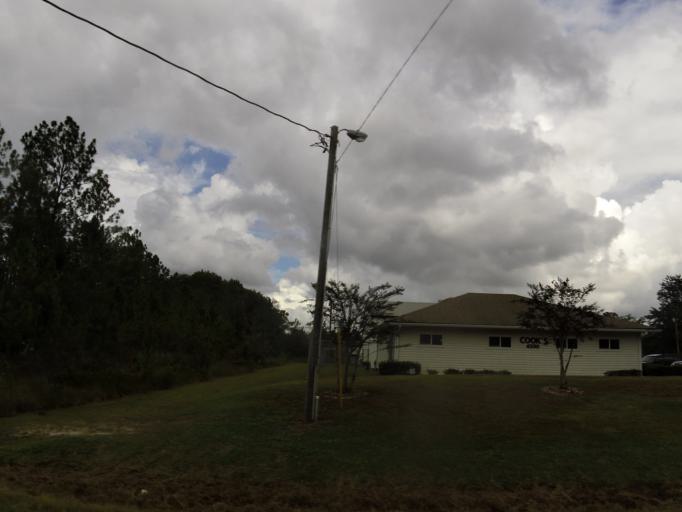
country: US
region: Florida
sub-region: Clay County
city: Middleburg
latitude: 30.0654
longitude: -81.9167
